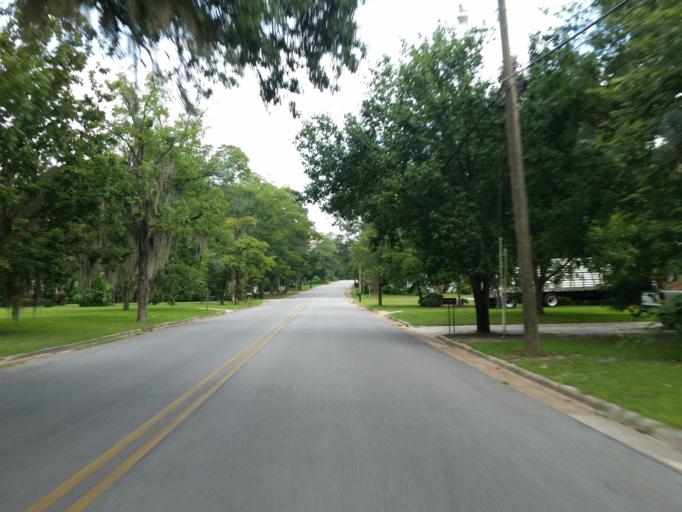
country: US
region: Georgia
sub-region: Cook County
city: Adel
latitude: 31.1350
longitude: -83.4191
